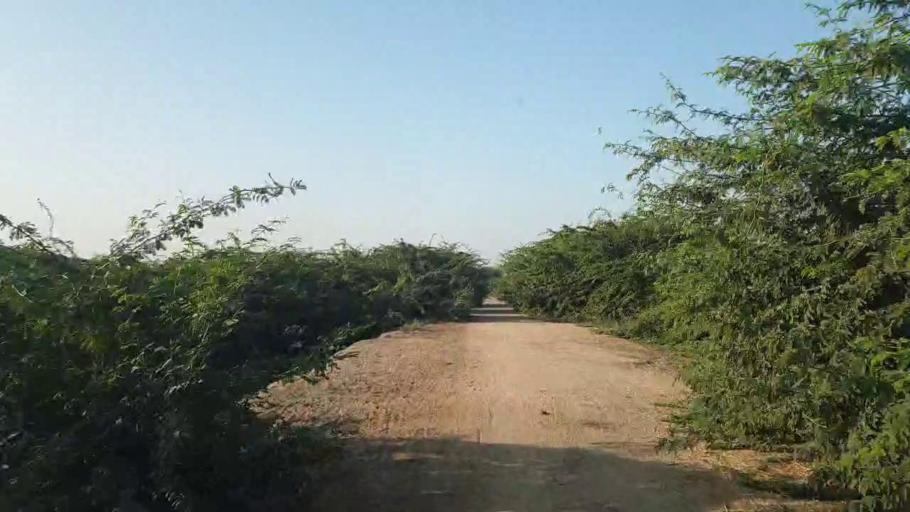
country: PK
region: Sindh
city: Badin
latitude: 24.6025
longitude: 68.7777
